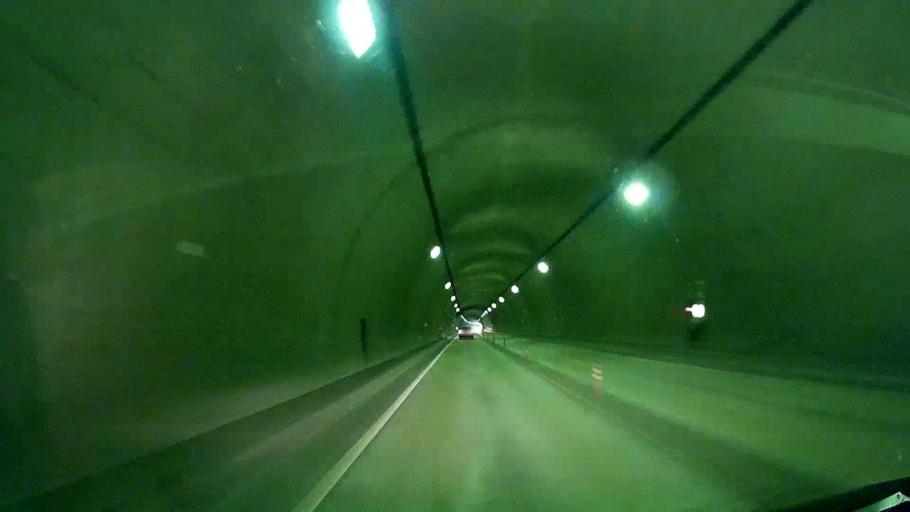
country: JP
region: Shizuoka
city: Shizuoka-shi
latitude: 35.0239
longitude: 138.3842
